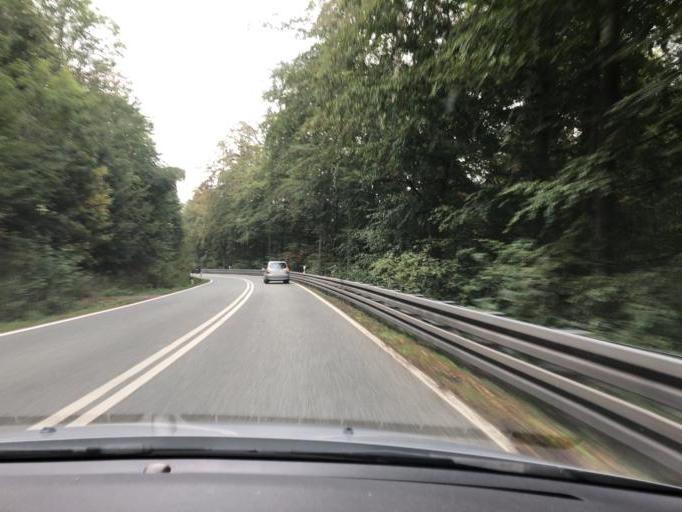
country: DE
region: Saxony-Anhalt
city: Kelbra
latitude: 51.4233
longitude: 11.0561
